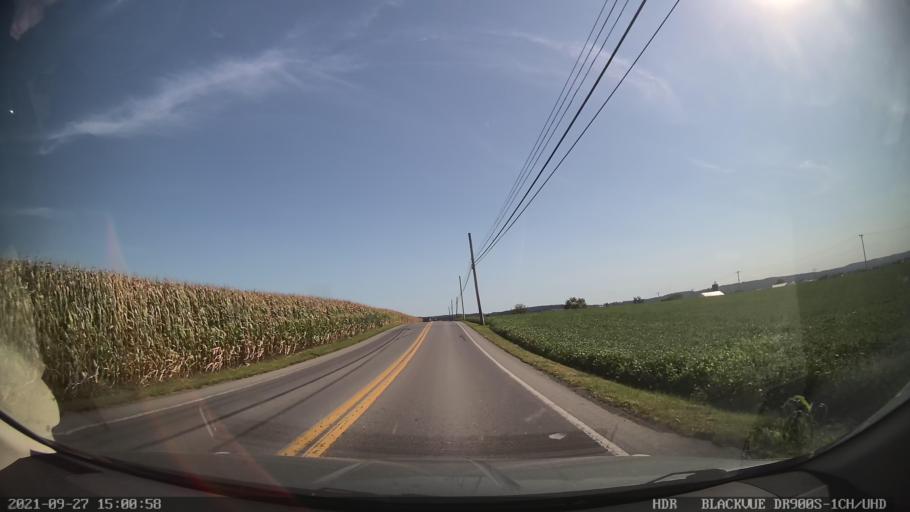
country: US
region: Pennsylvania
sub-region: Berks County
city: Kutztown
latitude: 40.5001
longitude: -75.7663
